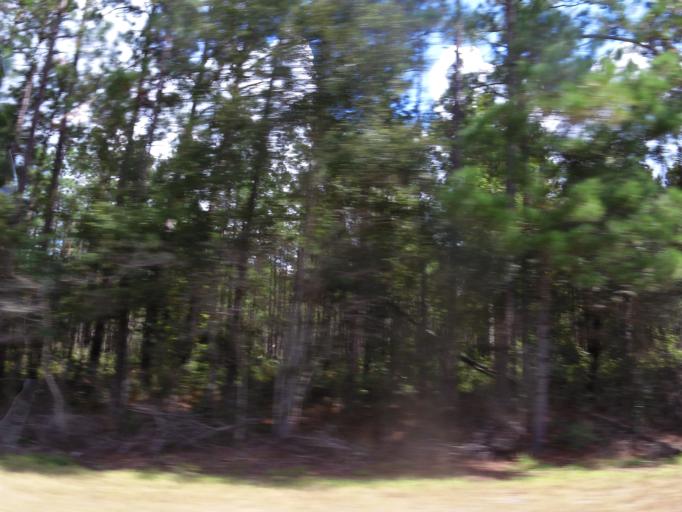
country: US
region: Georgia
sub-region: Charlton County
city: Folkston
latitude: 30.9933
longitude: -82.0261
